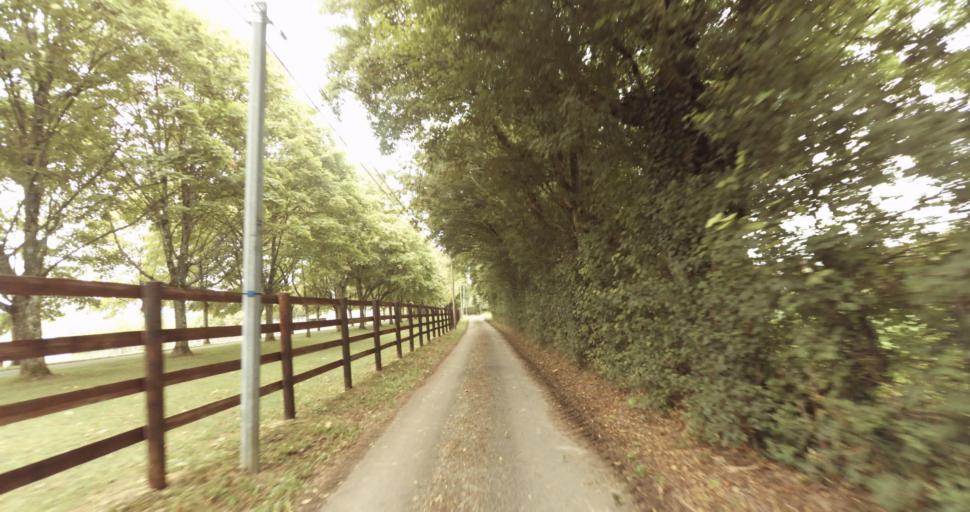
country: FR
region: Lower Normandy
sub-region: Departement de l'Orne
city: Sainte-Gauburge-Sainte-Colombe
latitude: 48.7383
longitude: 0.3598
